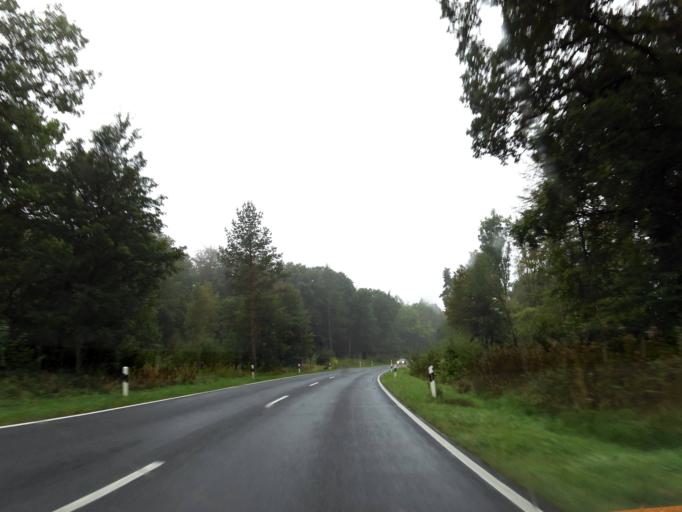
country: DE
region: Lower Saxony
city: Walkenried
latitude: 51.5943
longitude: 10.5896
